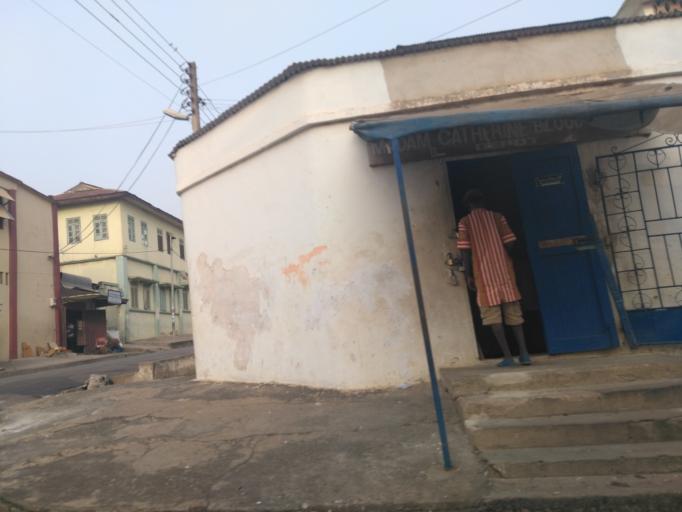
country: GH
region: Ashanti
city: Kumasi
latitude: 6.6847
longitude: -1.6124
